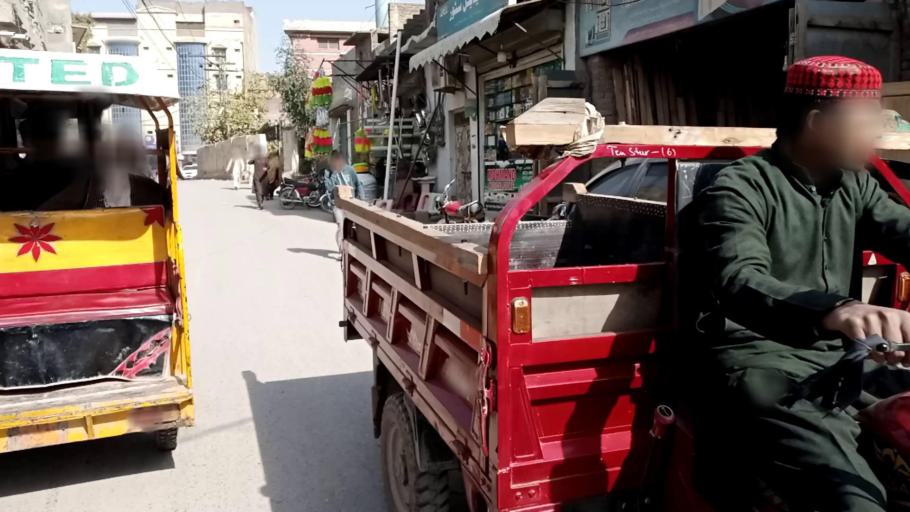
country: PK
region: Khyber Pakhtunkhwa
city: Peshawar
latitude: 34.0040
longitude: 71.5782
